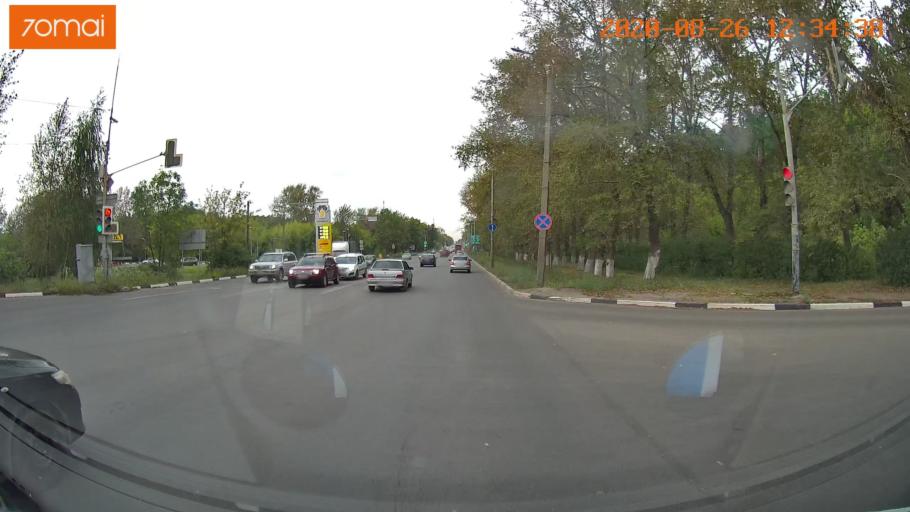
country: RU
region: Rjazan
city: Ryazan'
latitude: 54.5895
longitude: 39.7709
